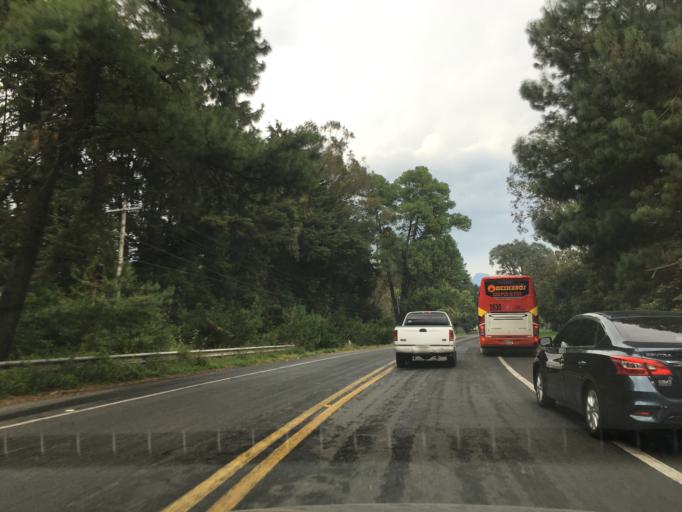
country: MX
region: Michoacan
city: Capacuaro
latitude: 19.5223
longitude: -102.0780
